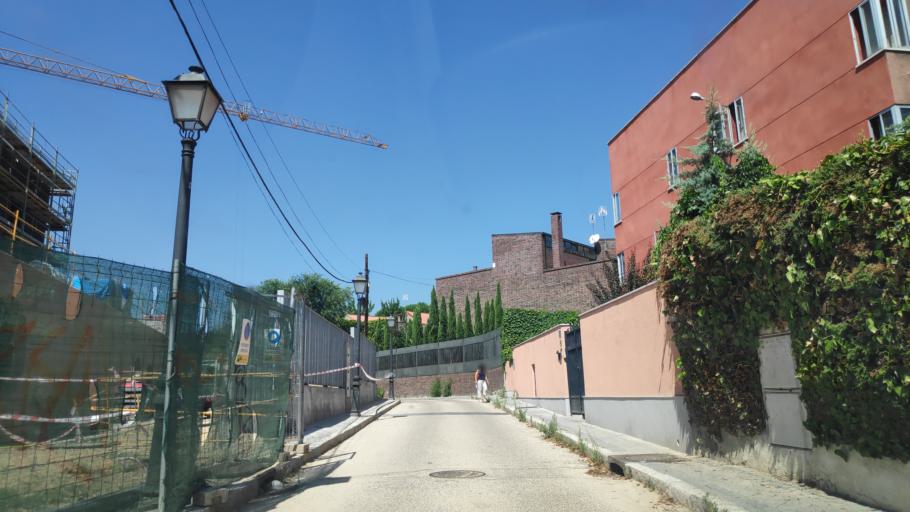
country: ES
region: Madrid
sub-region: Provincia de Madrid
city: Pozuelo de Alarcon
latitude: 40.4587
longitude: -3.7863
